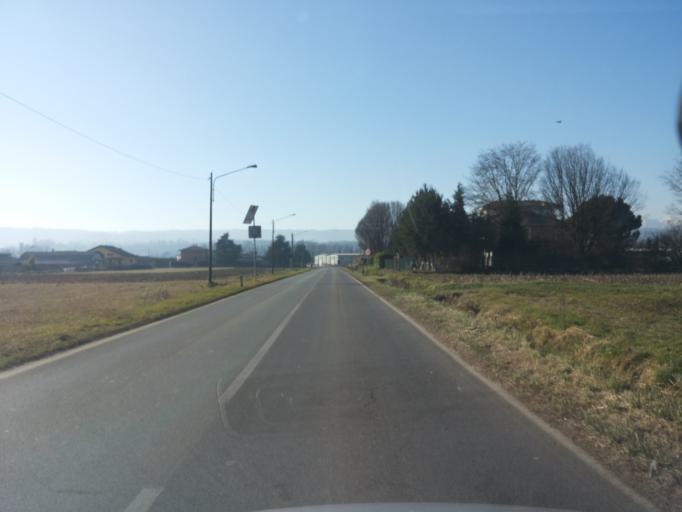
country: IT
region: Piedmont
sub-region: Provincia di Biella
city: Vergnasco
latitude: 45.4843
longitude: 8.0786
